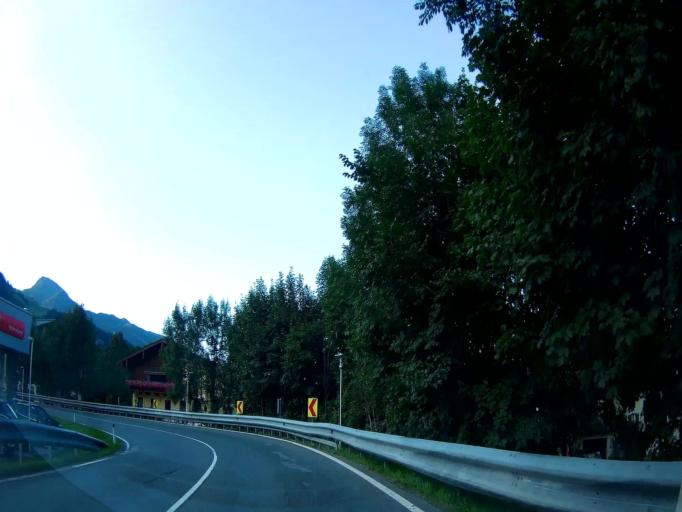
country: AT
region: Salzburg
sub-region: Politischer Bezirk Zell am See
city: Lofer
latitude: 47.5852
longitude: 12.7002
